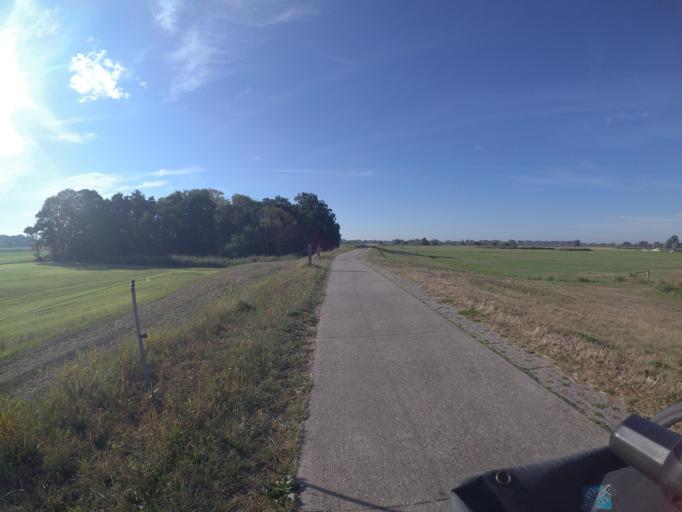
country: NL
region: Overijssel
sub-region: Gemeente Zwartewaterland
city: Hasselt
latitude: 52.5652
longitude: 6.1101
